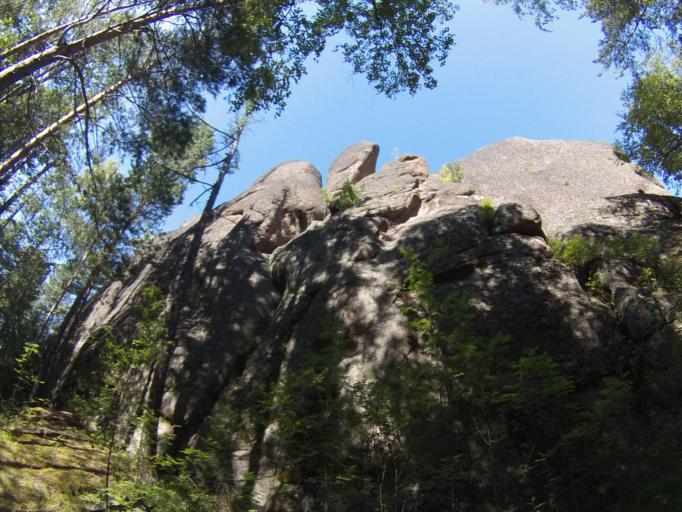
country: RU
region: Krasnoyarskiy
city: Krasnoyarsk
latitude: 55.9272
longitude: 92.7598
